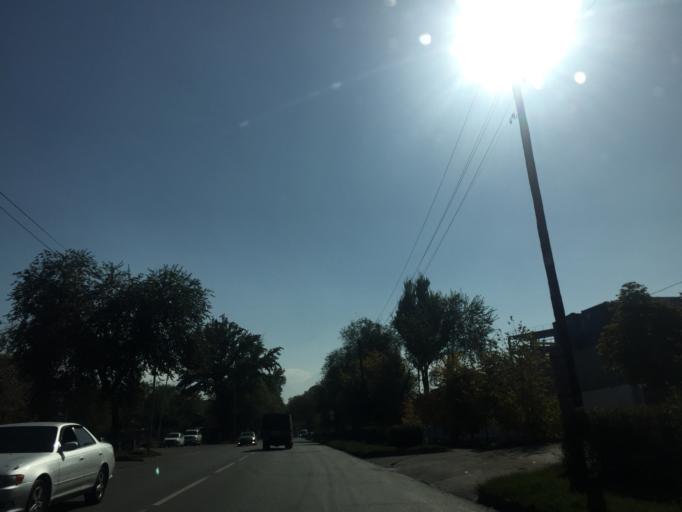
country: KZ
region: Almaty Qalasy
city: Almaty
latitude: 43.2613
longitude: 76.9108
